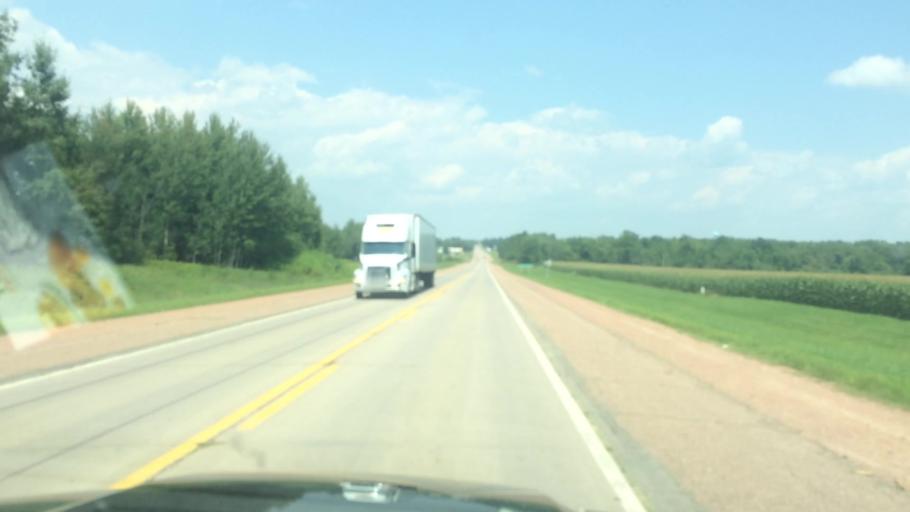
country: US
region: Wisconsin
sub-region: Clark County
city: Colby
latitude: 44.8845
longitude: -90.3154
